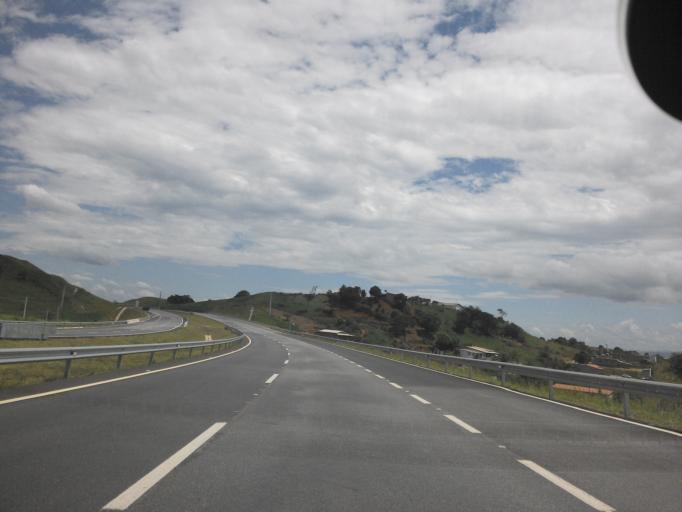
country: BR
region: Sao Paulo
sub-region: Taubate
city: Taubate
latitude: -23.0926
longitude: -45.5804
